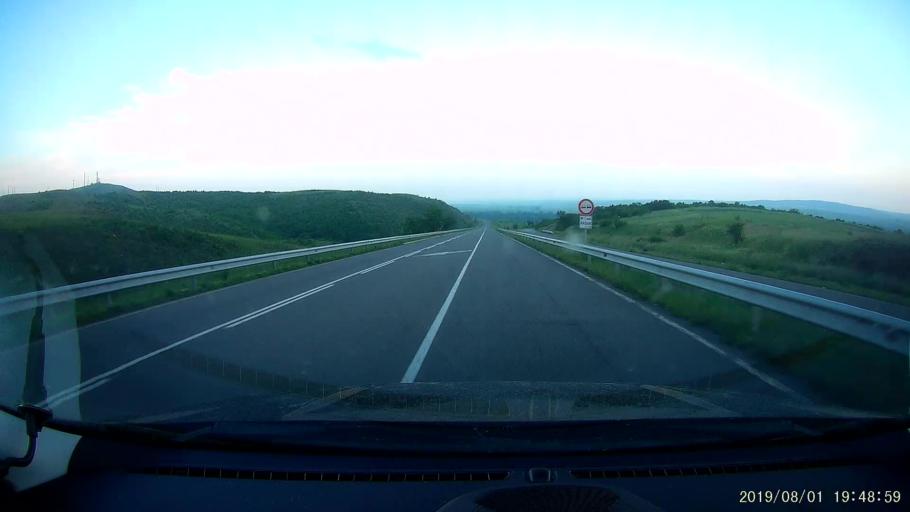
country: BG
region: Burgas
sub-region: Obshtina Karnobat
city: Karnobat
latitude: 42.6290
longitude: 26.9432
